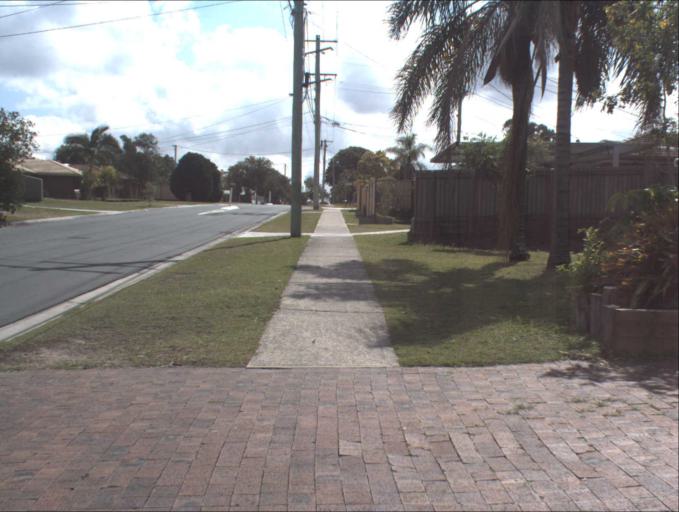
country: AU
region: Queensland
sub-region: Brisbane
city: Sunnybank Hills
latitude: -27.6605
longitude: 153.0567
